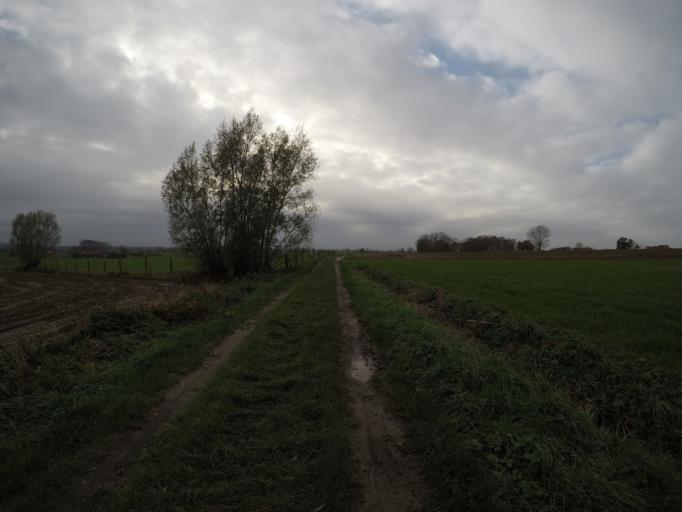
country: BE
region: Flanders
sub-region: Provincie West-Vlaanderen
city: Wervik
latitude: 50.8101
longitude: 3.0174
